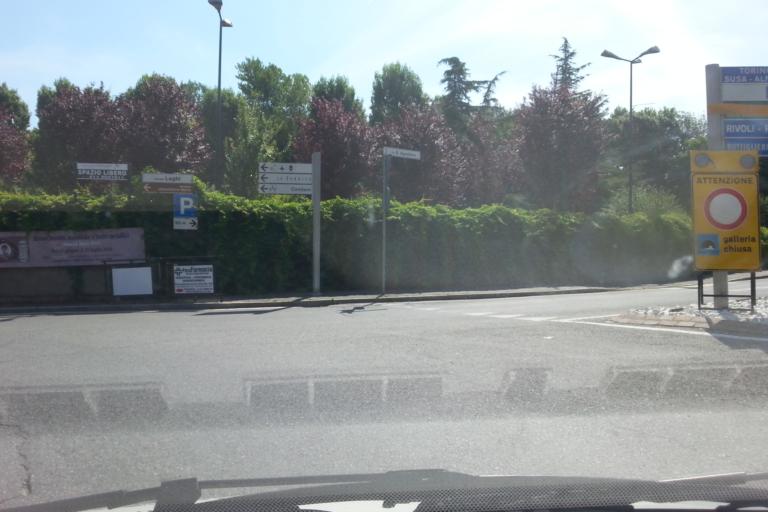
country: IT
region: Piedmont
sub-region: Provincia di Torino
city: Avigliana
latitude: 45.0762
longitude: 7.4018
